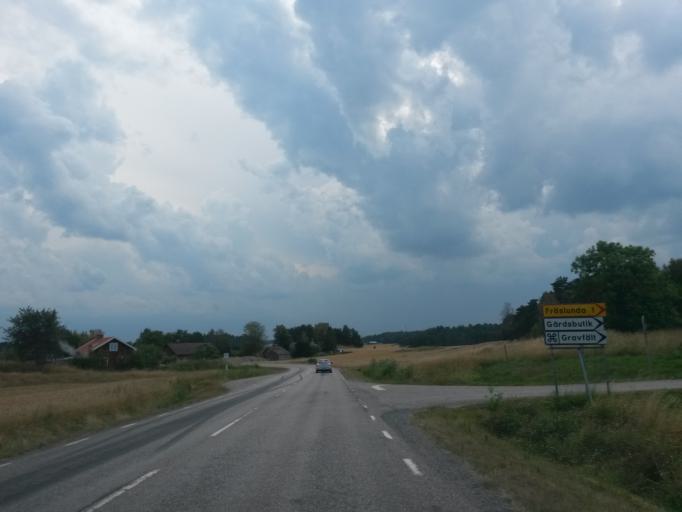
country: SE
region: Vaestra Goetaland
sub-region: Lidkopings Kommun
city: Lidkoping
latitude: 58.5867
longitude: 13.1187
